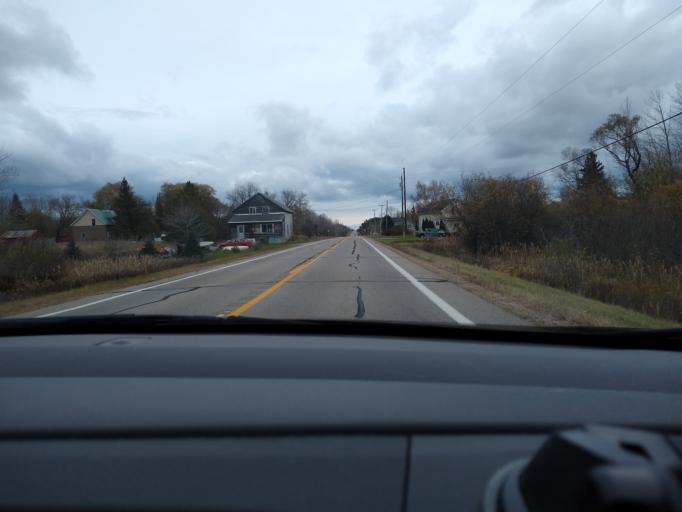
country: US
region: Michigan
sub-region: Delta County
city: Escanaba
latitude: 45.7529
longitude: -87.2865
